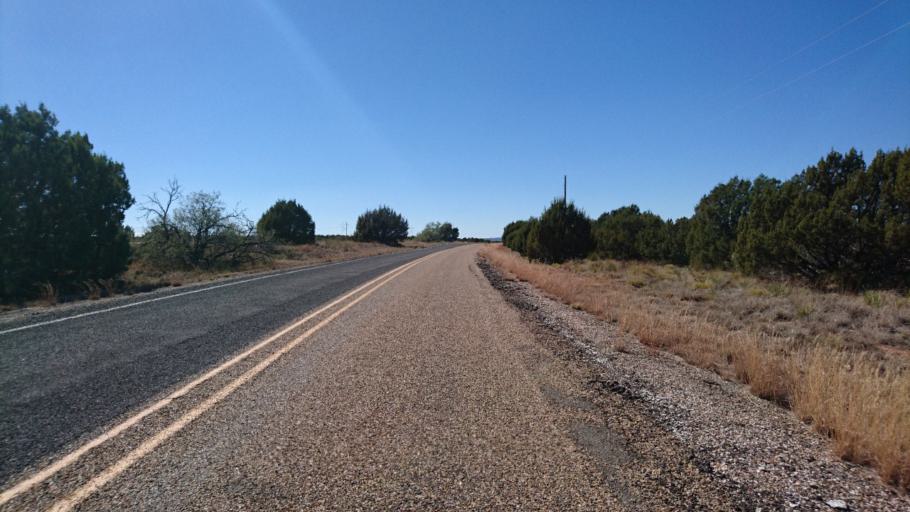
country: US
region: New Mexico
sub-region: Quay County
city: Tucumcari
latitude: 35.0670
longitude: -104.1834
